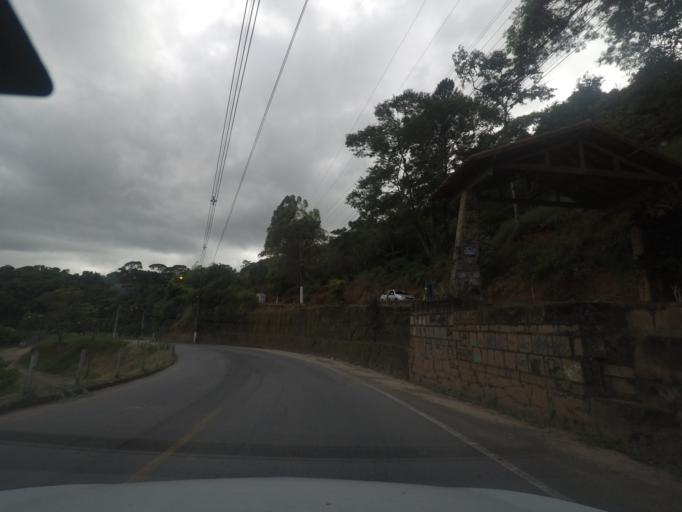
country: BR
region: Rio de Janeiro
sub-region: Teresopolis
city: Teresopolis
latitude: -22.3949
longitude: -42.9581
